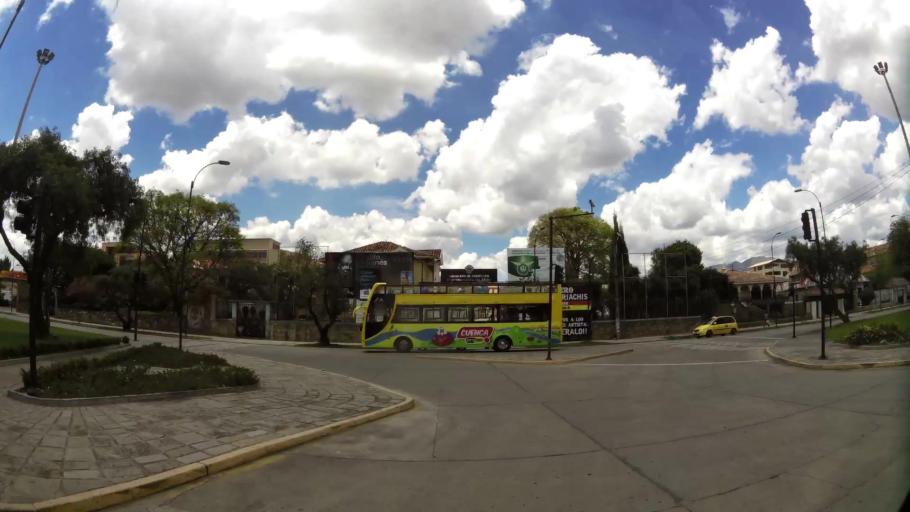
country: EC
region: Azuay
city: Cuenca
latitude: -2.9051
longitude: -79.0068
